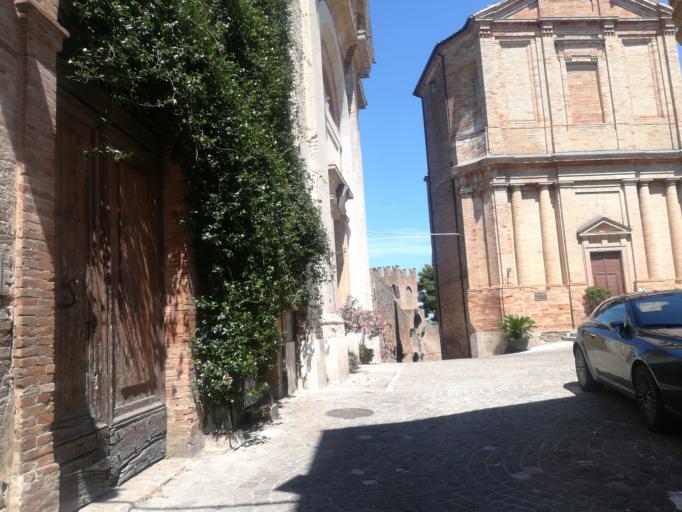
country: IT
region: The Marches
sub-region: Provincia di Ancona
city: Corinaldo
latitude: 43.6501
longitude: 13.0468
